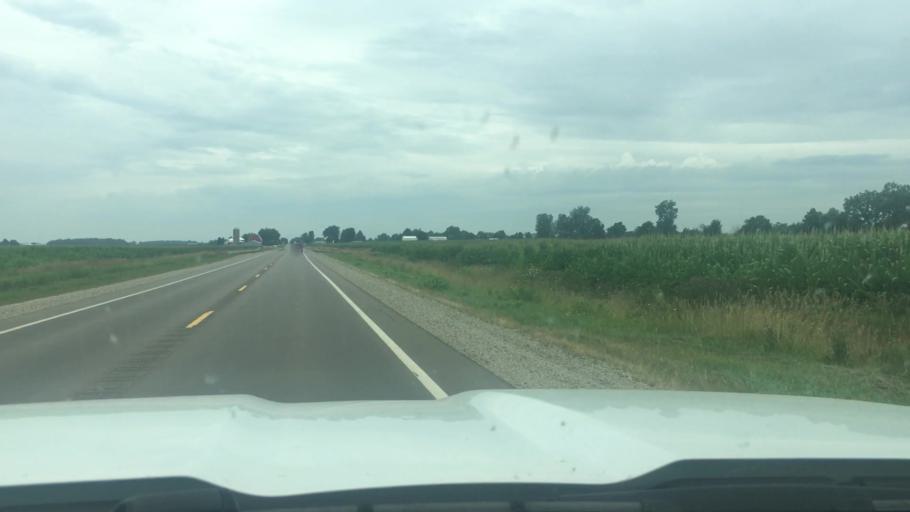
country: US
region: Michigan
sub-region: Clinton County
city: Fowler
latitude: 43.0017
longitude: -84.6686
